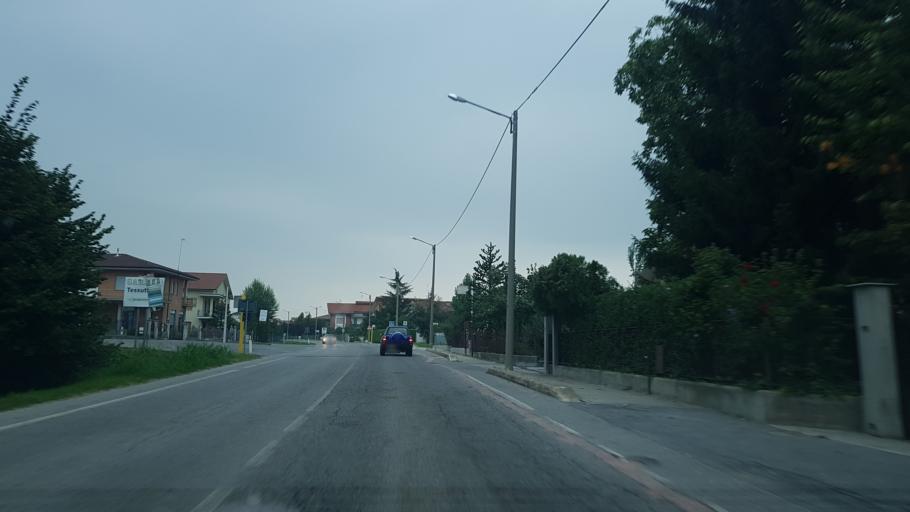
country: IT
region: Piedmont
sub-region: Provincia di Cuneo
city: Villanova Mondovi
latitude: 44.3459
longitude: 7.7764
